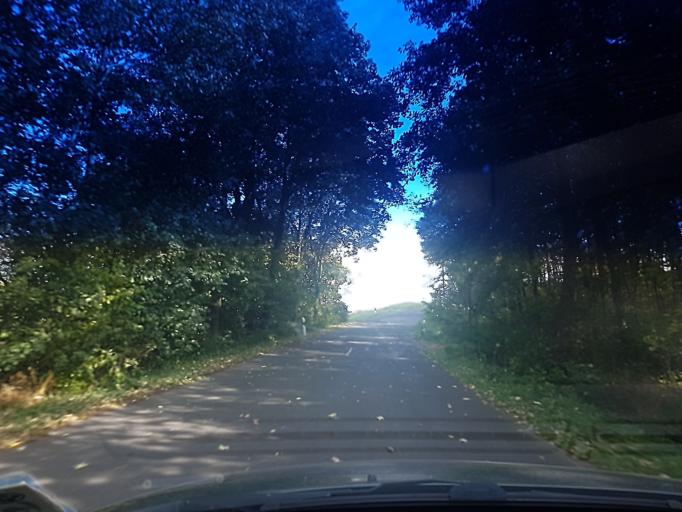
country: DE
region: Bavaria
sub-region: Upper Franconia
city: Schlusselfeld
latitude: 49.7906
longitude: 10.6521
